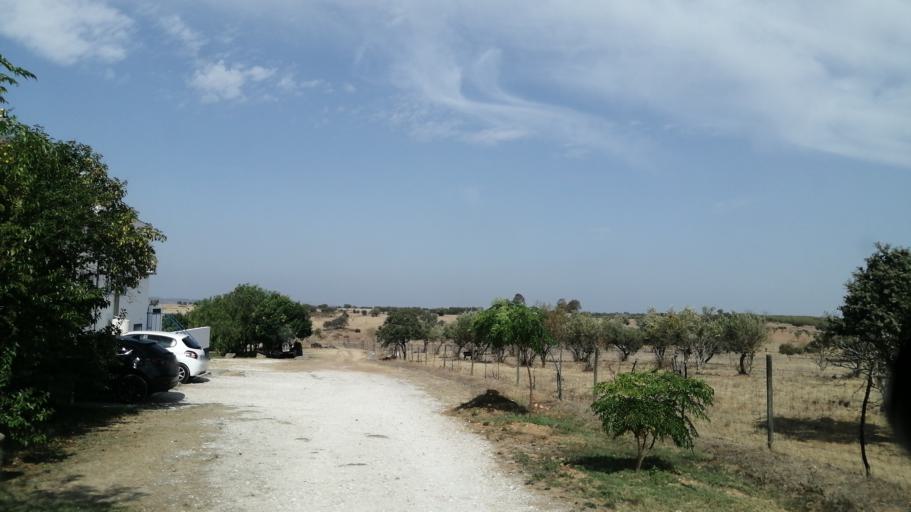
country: PT
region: Evora
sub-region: Mourao
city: Mourao
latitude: 38.3944
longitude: -7.3187
